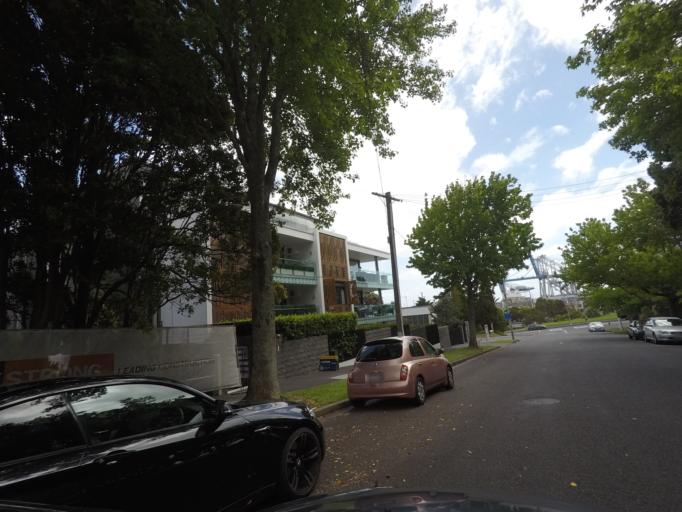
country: NZ
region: Auckland
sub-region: Auckland
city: Auckland
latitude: -36.8496
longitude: 174.7845
